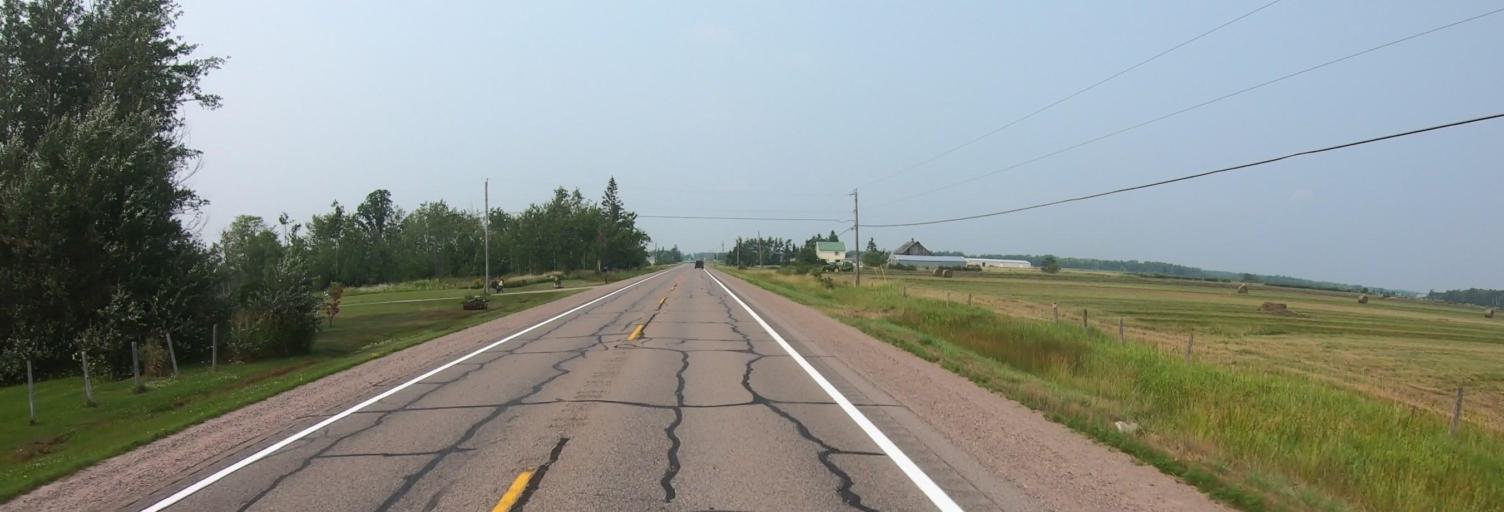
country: US
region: Michigan
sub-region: Chippewa County
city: Sault Ste. Marie
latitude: 46.4391
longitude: -84.3536
